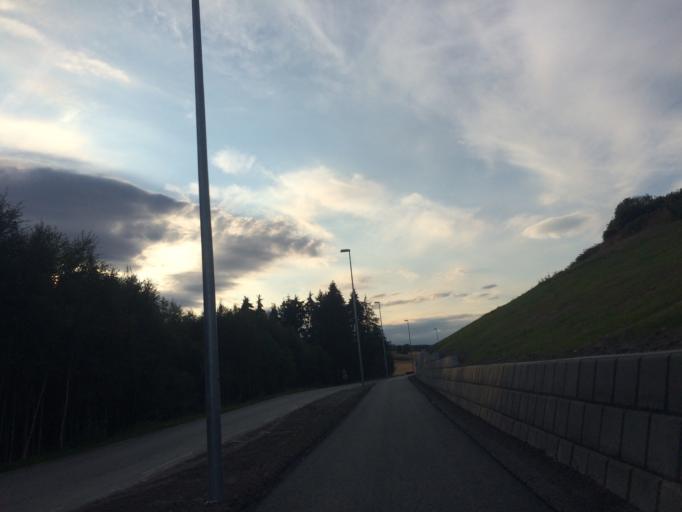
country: NO
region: Akershus
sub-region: Ski
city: Ski
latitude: 59.6848
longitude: 10.8713
